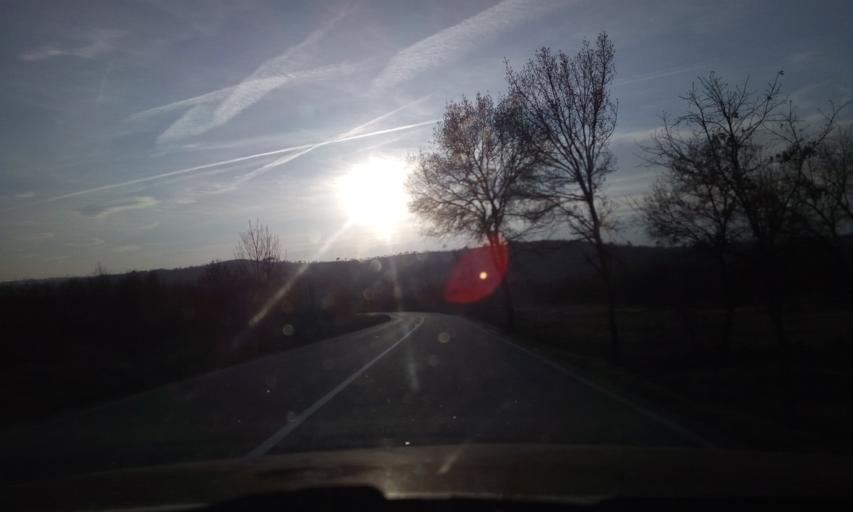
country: PT
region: Guarda
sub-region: Pinhel
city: Pinhel
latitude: 40.6009
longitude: -7.0261
